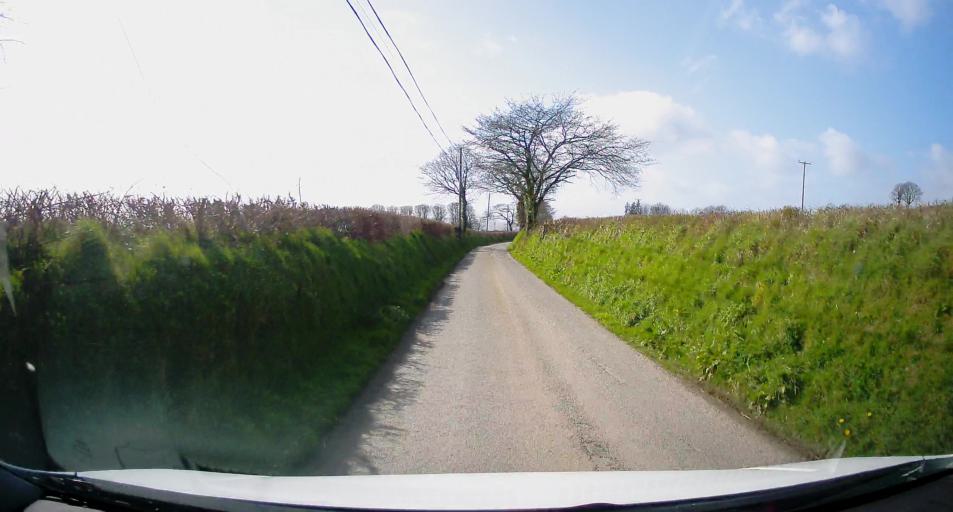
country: GB
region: Wales
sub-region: County of Ceredigion
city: Aberporth
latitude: 52.0731
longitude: -4.5521
